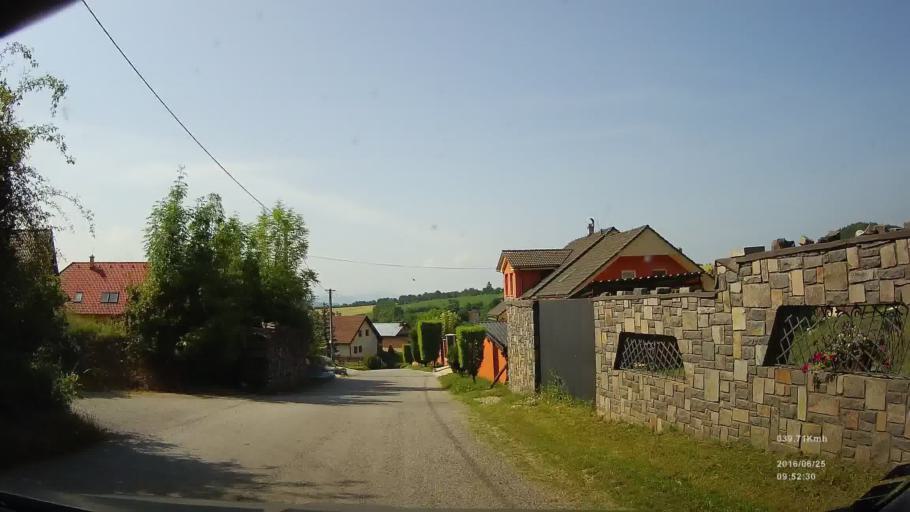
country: SK
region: Banskobystricky
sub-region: Okres Banska Bystrica
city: Banska Bystrica
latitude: 48.7017
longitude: 19.2150
